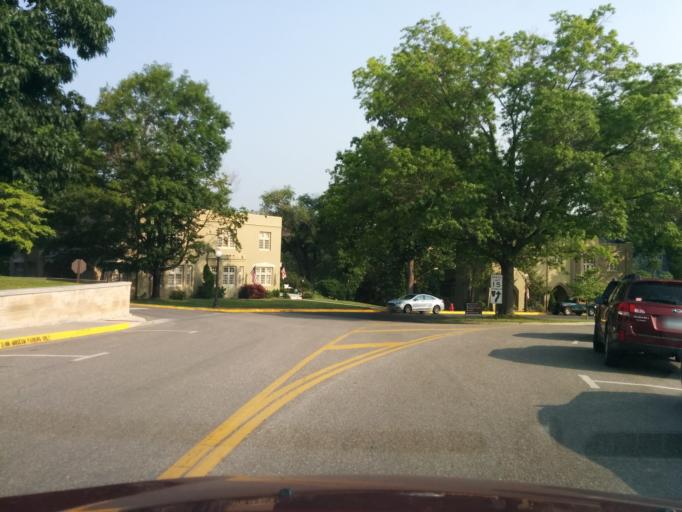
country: US
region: Virginia
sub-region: City of Lexington
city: Lexington
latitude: 37.7904
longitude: -79.4398
